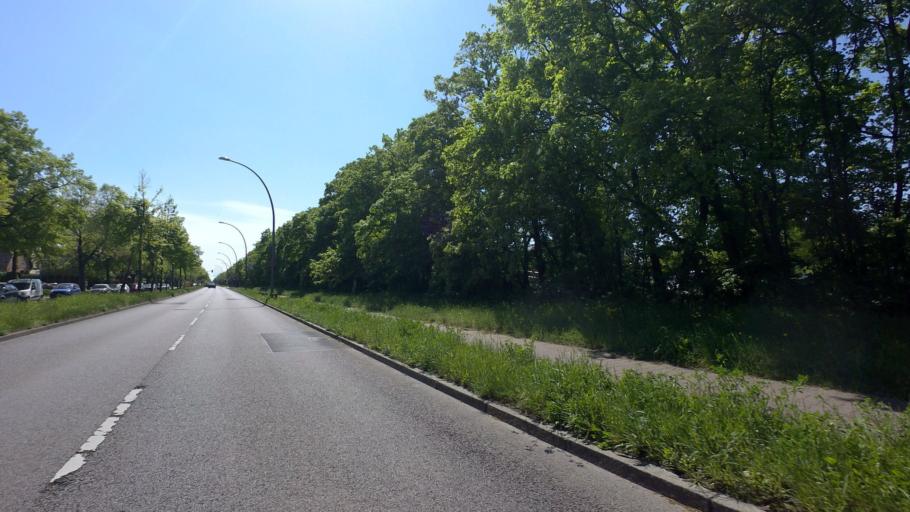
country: DE
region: Brandenburg
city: Schonefeld
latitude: 52.4060
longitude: 13.5090
